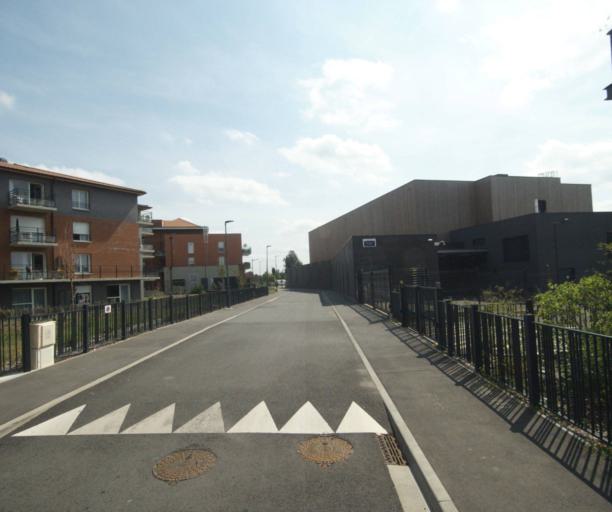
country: FR
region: Nord-Pas-de-Calais
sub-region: Departement du Nord
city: Hem
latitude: 50.6530
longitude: 3.1891
